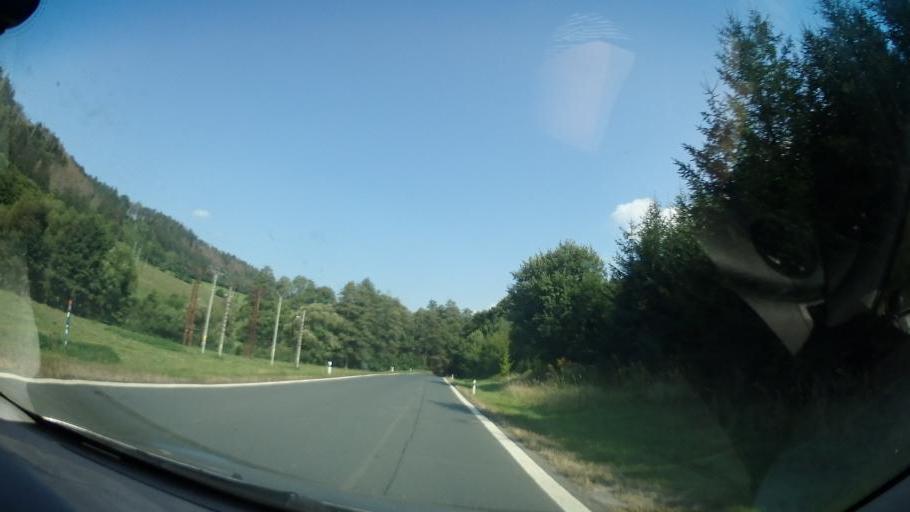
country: CZ
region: South Moravian
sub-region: Okres Brno-Venkov
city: Nedvedice
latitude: 49.5236
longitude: 16.3445
